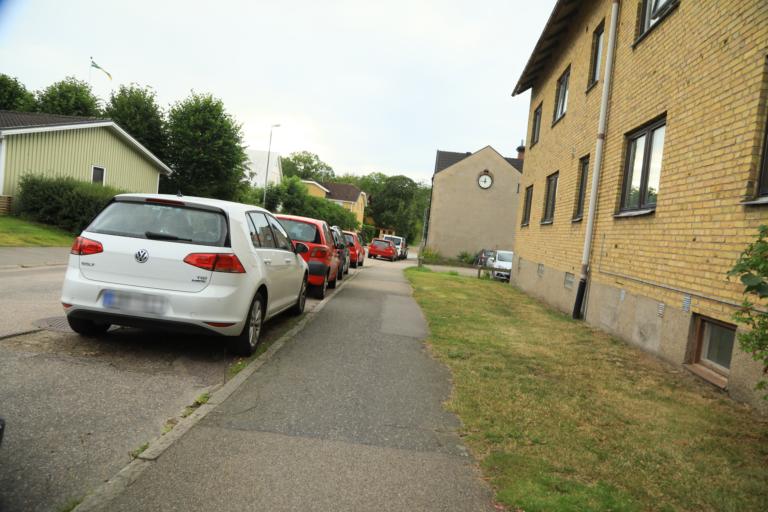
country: SE
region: Halland
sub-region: Varbergs Kommun
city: Varberg
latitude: 57.1028
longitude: 12.2534
